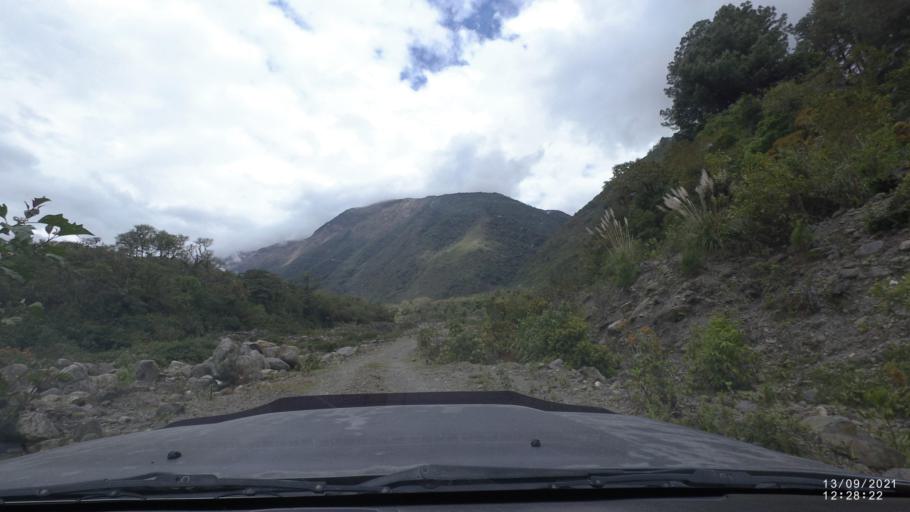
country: BO
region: Cochabamba
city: Colomi
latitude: -17.2579
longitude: -65.8144
